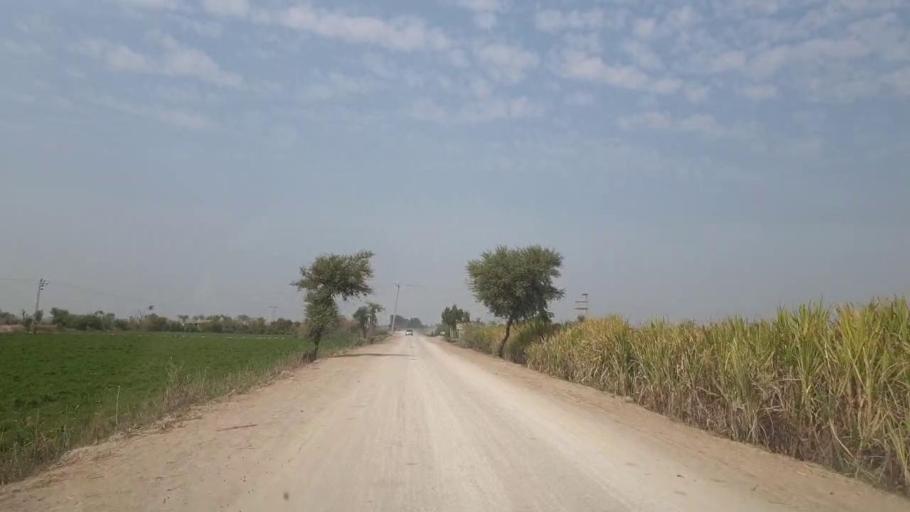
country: PK
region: Sindh
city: Mirpur Khas
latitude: 25.5445
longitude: 69.0831
